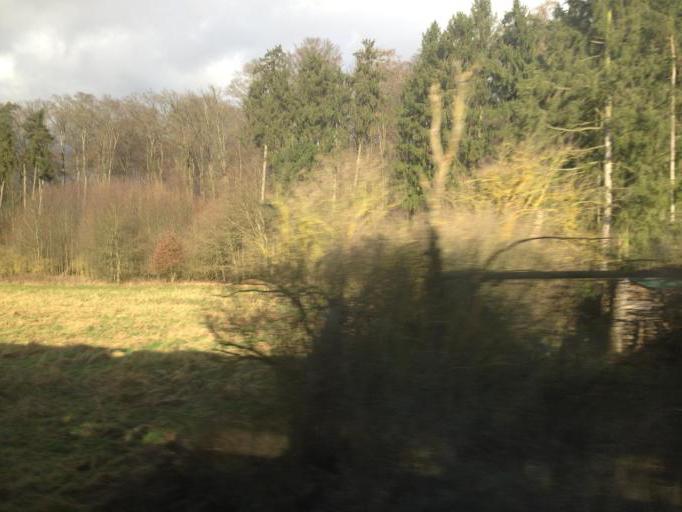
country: DE
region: Hesse
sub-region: Regierungsbezirk Giessen
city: Hungen
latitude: 50.4858
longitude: 8.8728
